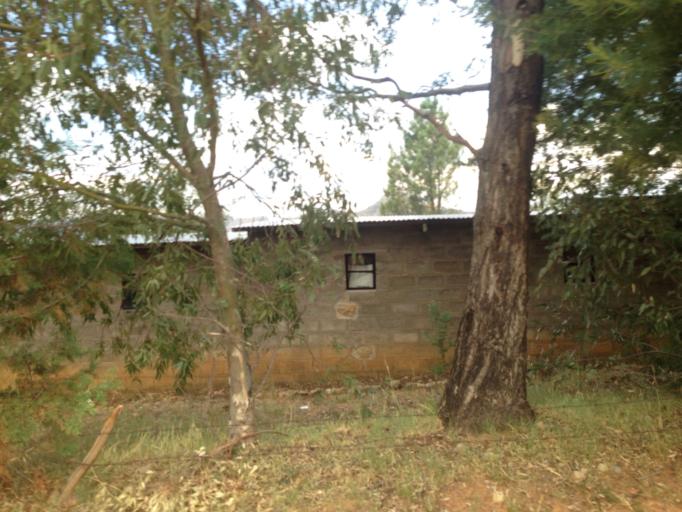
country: LS
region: Mafeteng
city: Mafeteng
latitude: -29.6927
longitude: 27.4320
